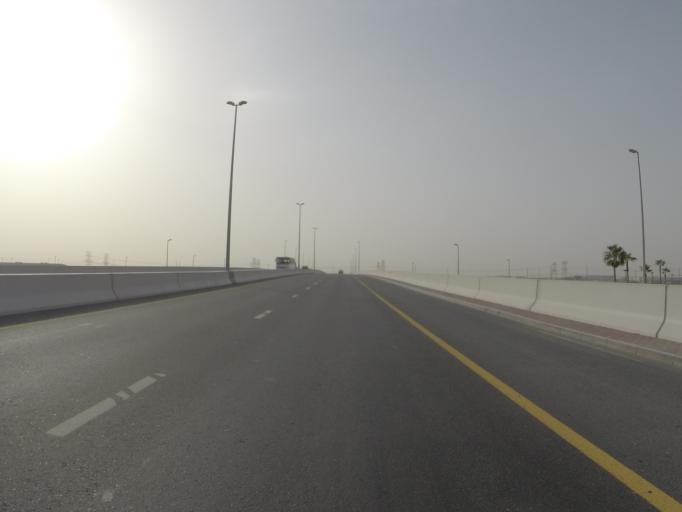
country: AE
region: Dubai
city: Dubai
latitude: 24.9590
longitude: 55.0981
